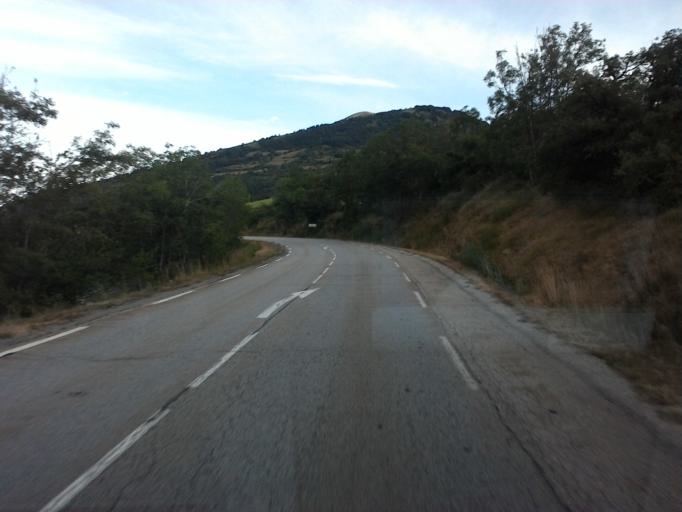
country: FR
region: Rhone-Alpes
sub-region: Departement de l'Isere
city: La Mure
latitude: 44.8312
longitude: 5.9189
